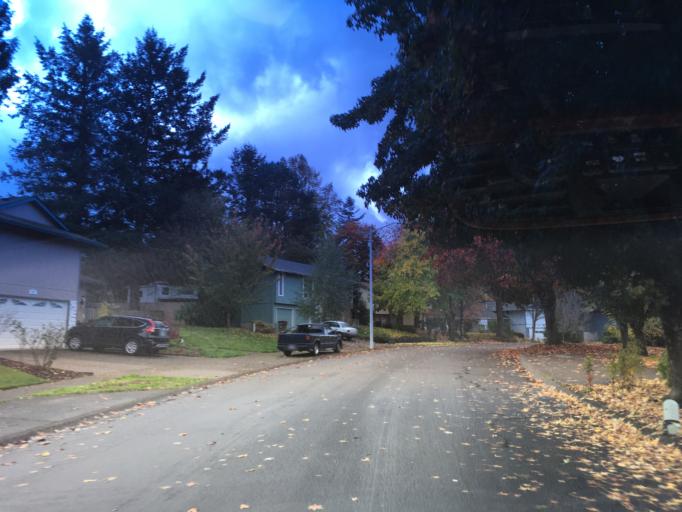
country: US
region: Oregon
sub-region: Multnomah County
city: Troutdale
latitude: 45.5126
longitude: -122.3819
